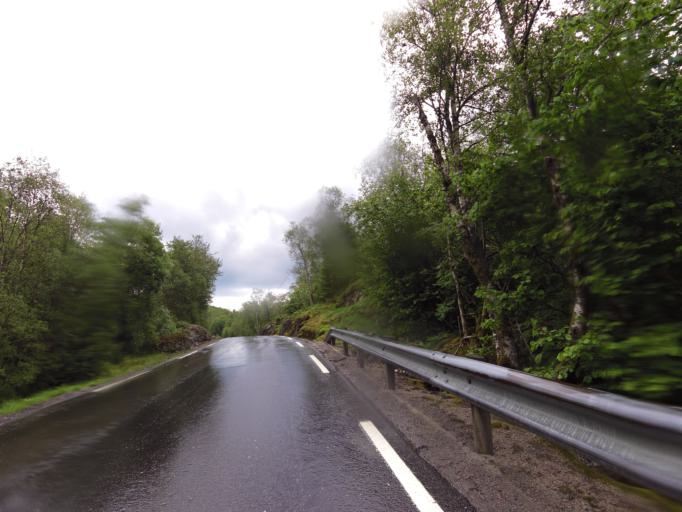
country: NO
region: Vest-Agder
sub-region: Lyngdal
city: Lyngdal
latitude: 58.1097
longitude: 7.0887
